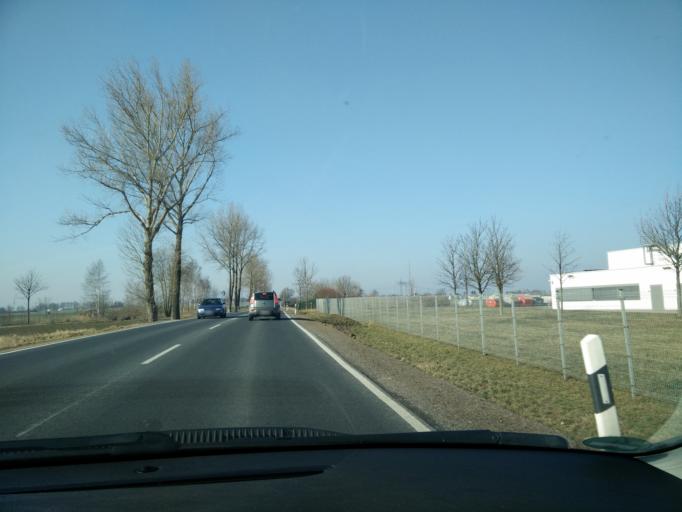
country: DE
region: Saxony
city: Wittgensdorf
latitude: 50.8659
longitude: 12.8484
